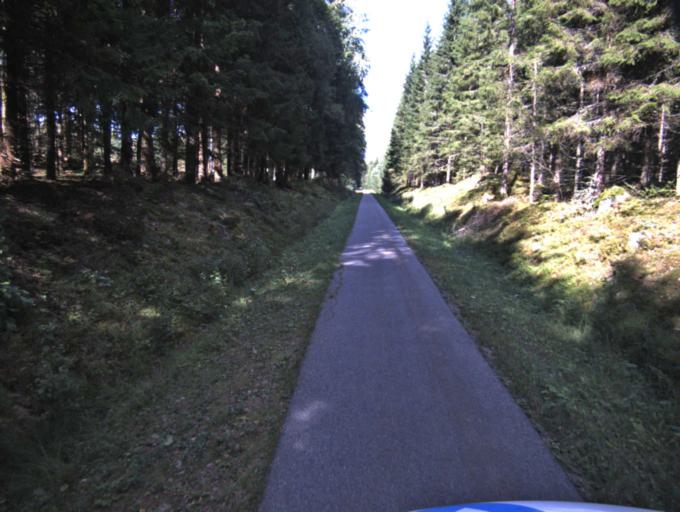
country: SE
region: Vaestra Goetaland
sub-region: Ulricehamns Kommun
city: Ulricehamn
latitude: 57.8255
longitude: 13.3458
